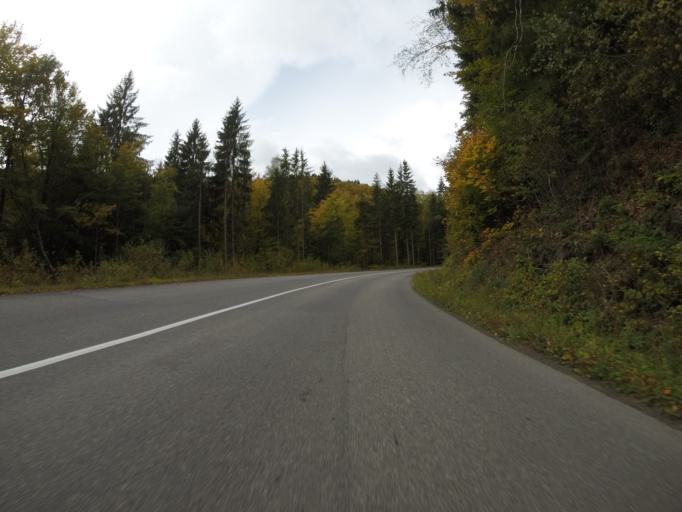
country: SK
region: Banskobystricky
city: Cierny Balog
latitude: 48.5985
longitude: 19.7051
